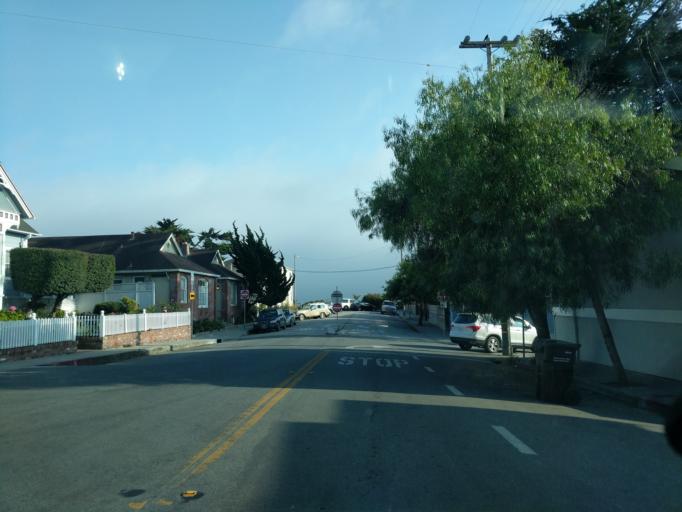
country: US
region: California
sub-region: Santa Cruz County
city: Twin Lakes
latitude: 36.9649
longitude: -122.0076
